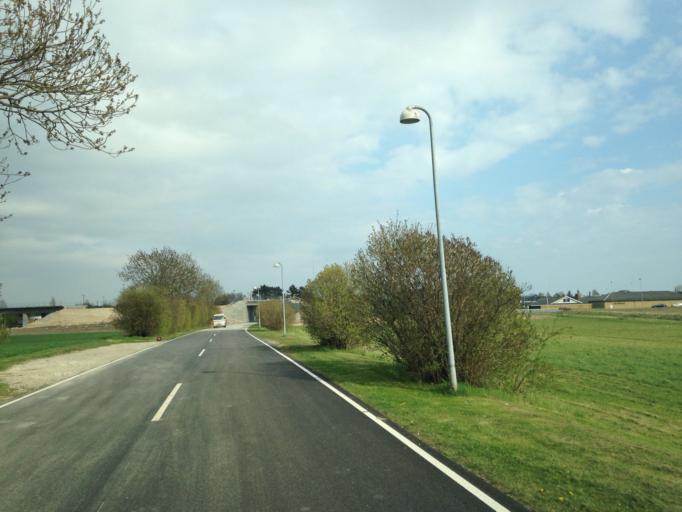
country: DK
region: Capital Region
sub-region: Ishoj Kommune
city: Ishoj
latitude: 55.6227
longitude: 12.3165
